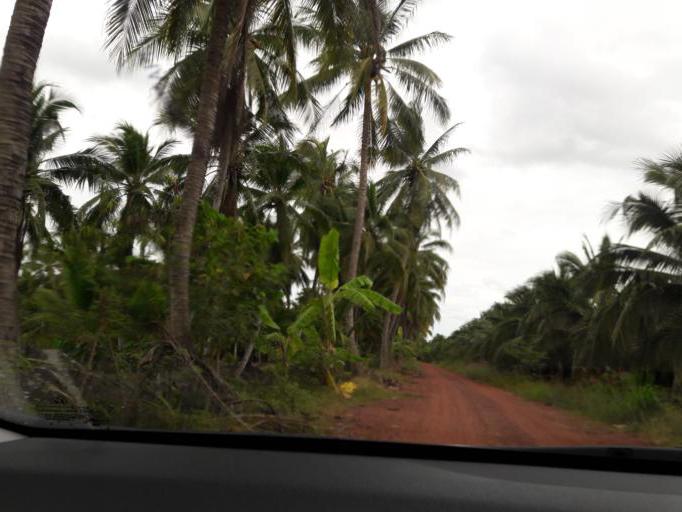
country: TH
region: Samut Sakhon
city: Ban Phaeo
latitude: 13.5471
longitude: 100.0380
